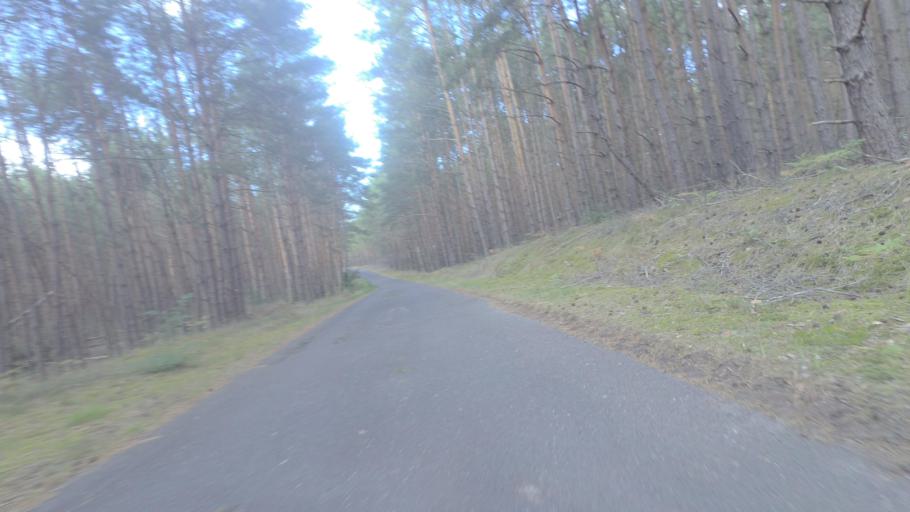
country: DE
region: Brandenburg
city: Munchehofe
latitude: 52.1705
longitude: 13.8823
